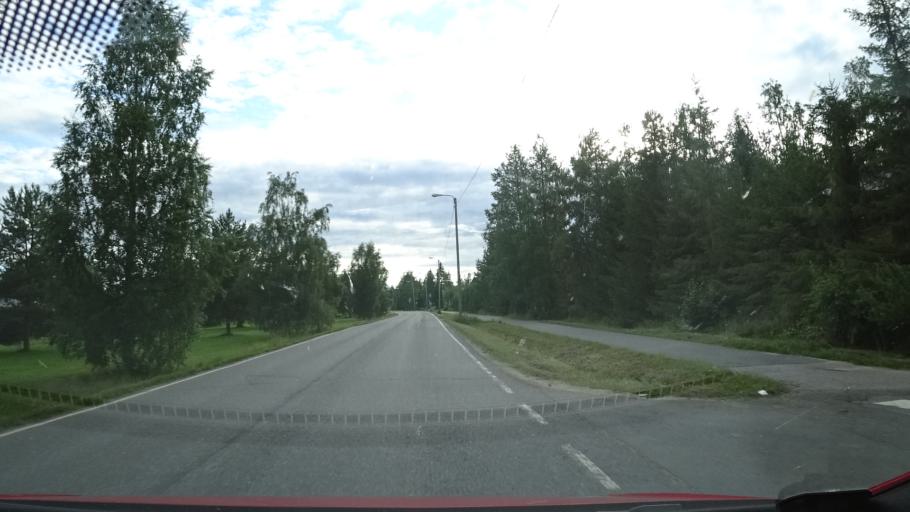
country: FI
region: Northern Ostrobothnia
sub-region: Oulu
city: Liminka
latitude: 64.8082
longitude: 25.4435
